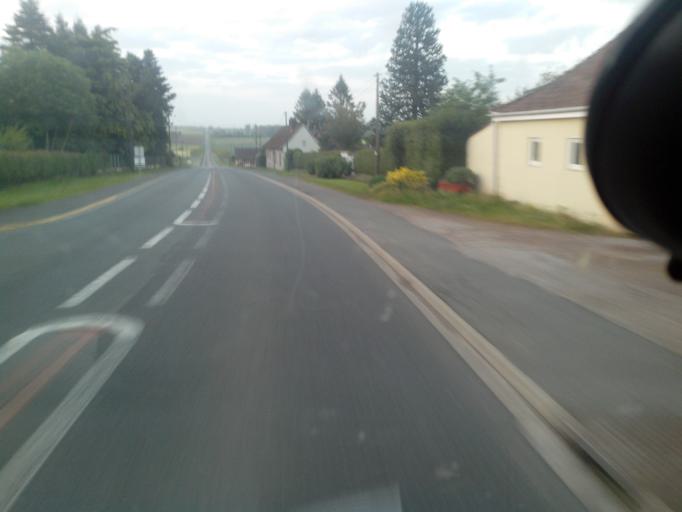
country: FR
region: Nord-Pas-de-Calais
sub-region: Departement du Pas-de-Calais
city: Marconnelle
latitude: 50.3138
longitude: 2.0128
